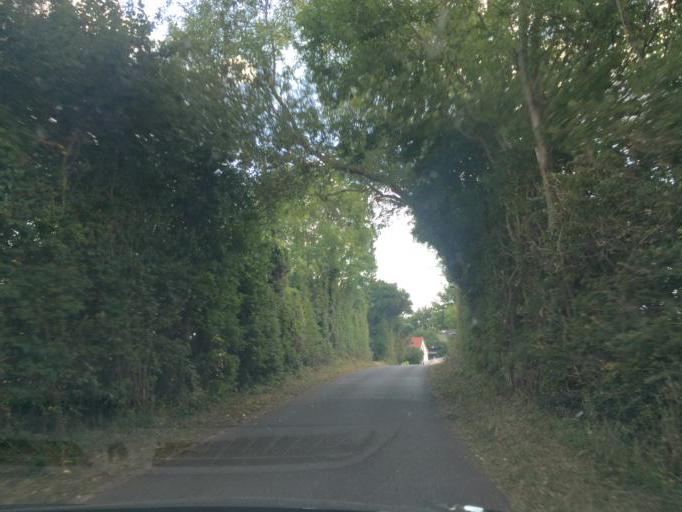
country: DK
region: South Denmark
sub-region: Assens Kommune
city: Glamsbjerg
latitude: 55.2102
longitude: 10.0054
